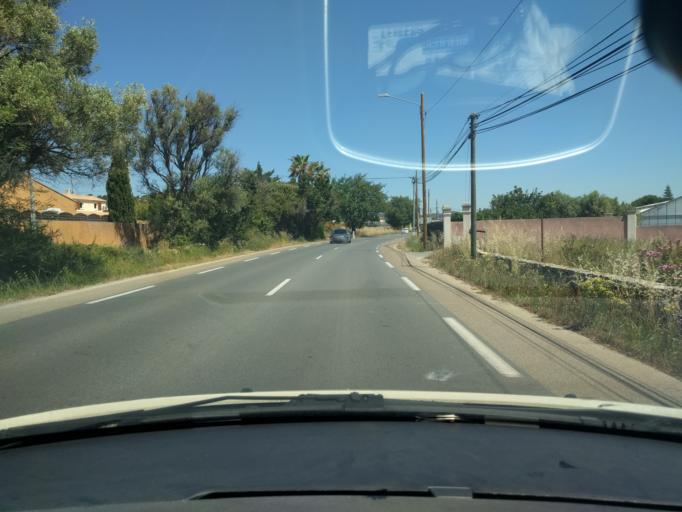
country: FR
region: Provence-Alpes-Cote d'Azur
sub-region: Departement du Var
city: Hyeres
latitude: 43.0887
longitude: 6.1289
